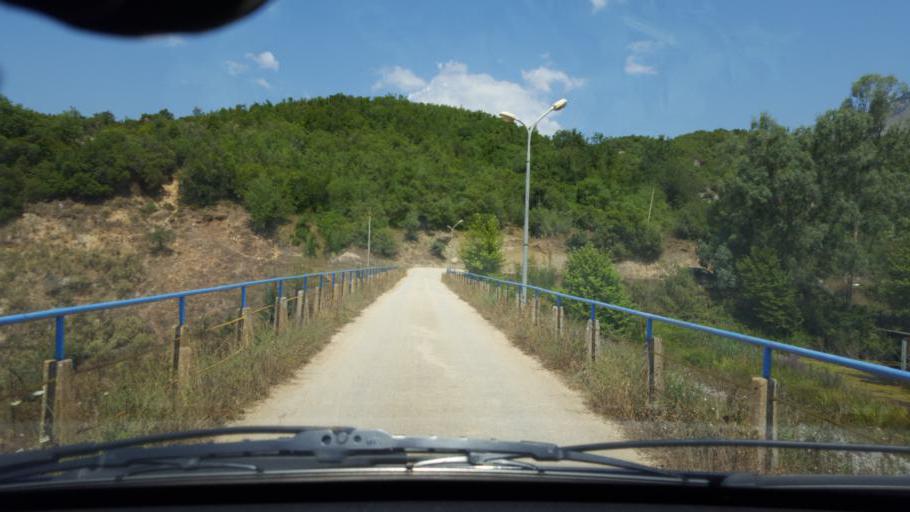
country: AL
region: Vlore
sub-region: Rrethi i Sarandes
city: Dhiver
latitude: 39.9180
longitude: 20.1850
